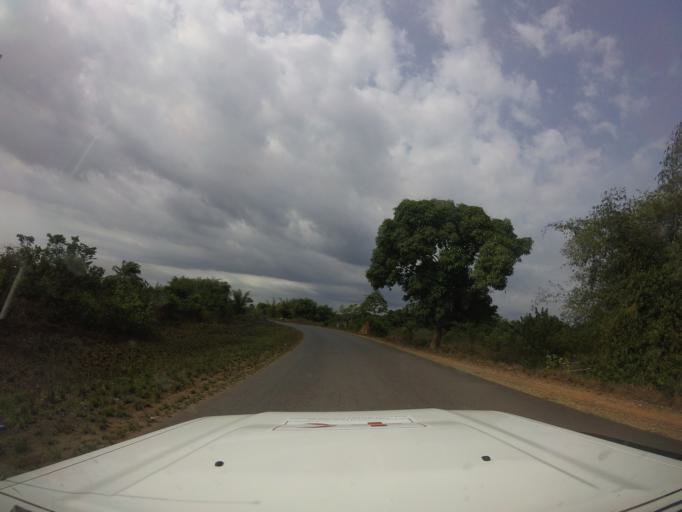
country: LR
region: Montserrado
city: Monrovia
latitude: 6.4936
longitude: -10.8107
